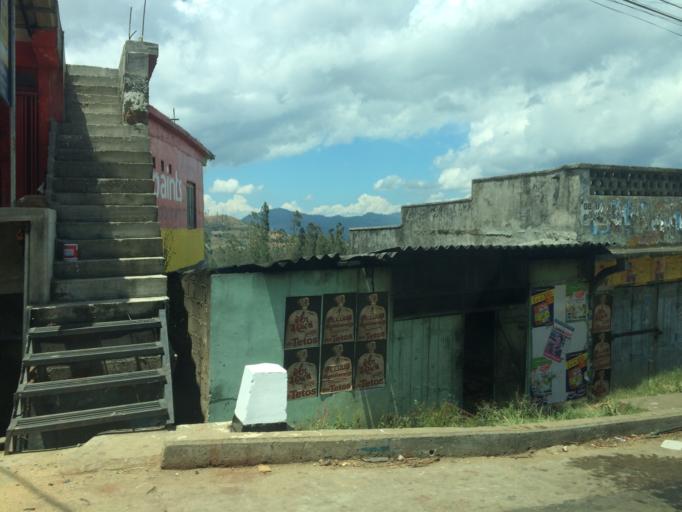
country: LK
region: Central
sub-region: Nuwara Eliya District
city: Nuwara Eliya
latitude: 6.9080
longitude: 80.8409
